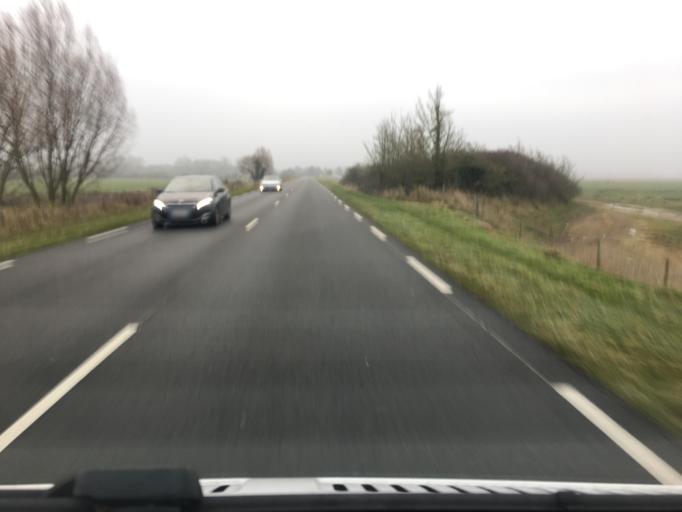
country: FR
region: Picardie
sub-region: Departement de la Somme
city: Le Crotoy
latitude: 50.2123
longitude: 1.6692
